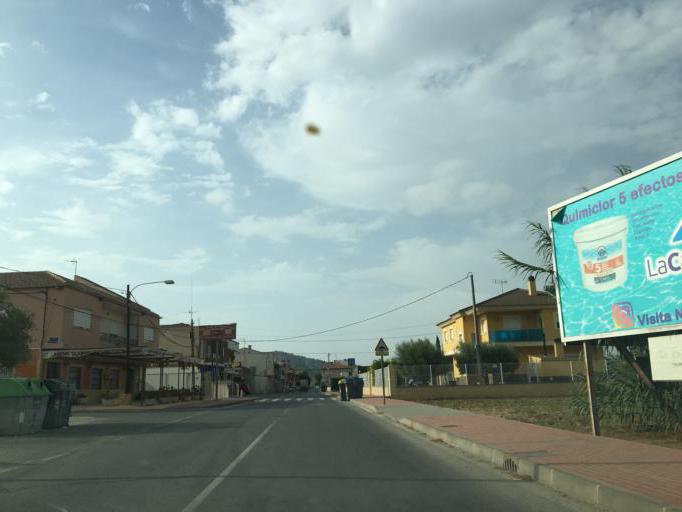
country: ES
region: Murcia
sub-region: Murcia
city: Murcia
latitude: 38.0117
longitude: -1.0814
